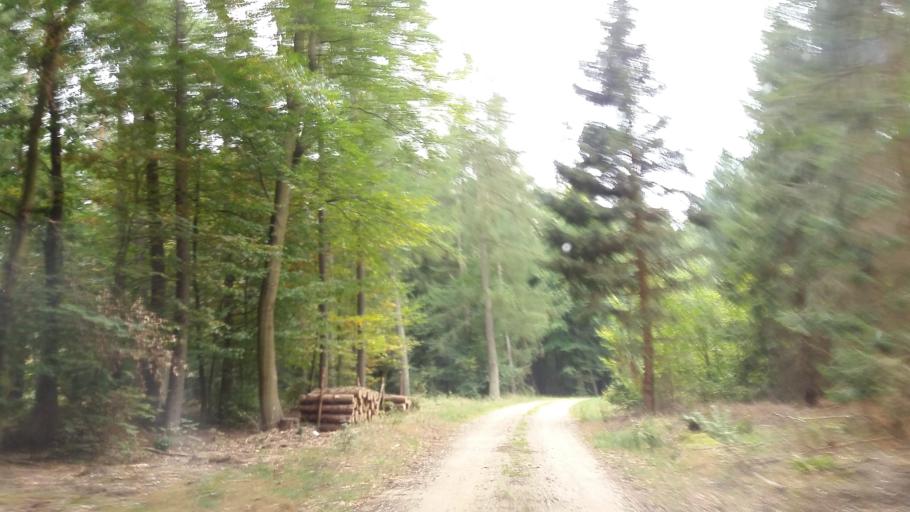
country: PL
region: West Pomeranian Voivodeship
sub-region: Powiat choszczenski
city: Pelczyce
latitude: 52.9634
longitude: 15.3388
